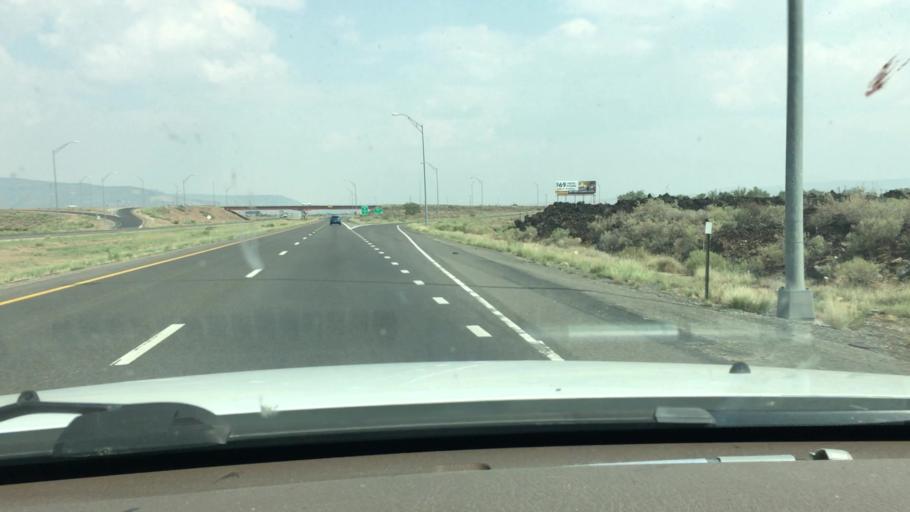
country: US
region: New Mexico
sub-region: Cibola County
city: Milan
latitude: 35.1557
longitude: -107.8782
